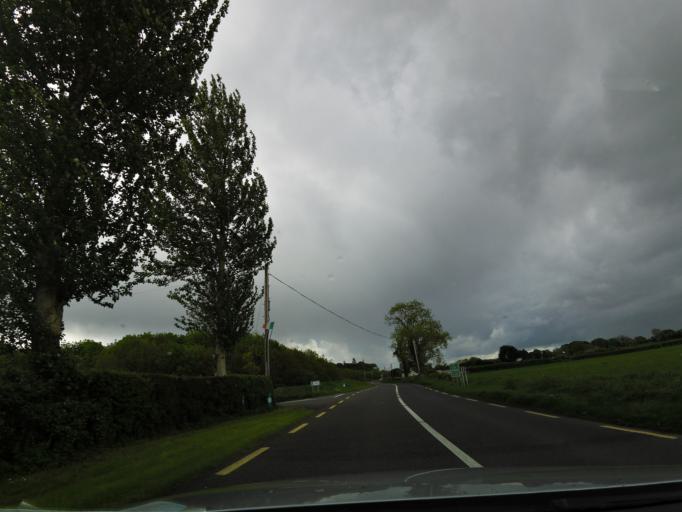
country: IE
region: Munster
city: Thurles
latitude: 52.7111
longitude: -7.8251
